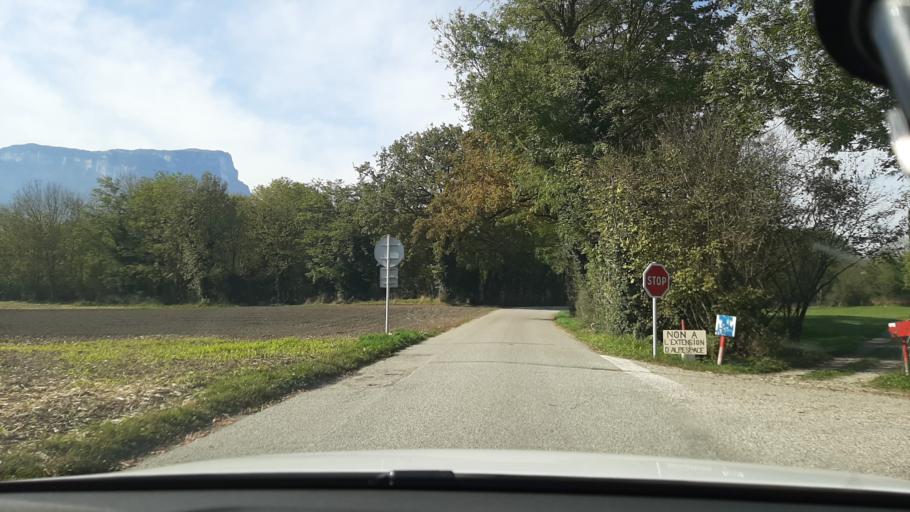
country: FR
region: Rhone-Alpes
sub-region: Departement de la Savoie
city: Montmelian
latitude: 45.4712
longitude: 6.0390
